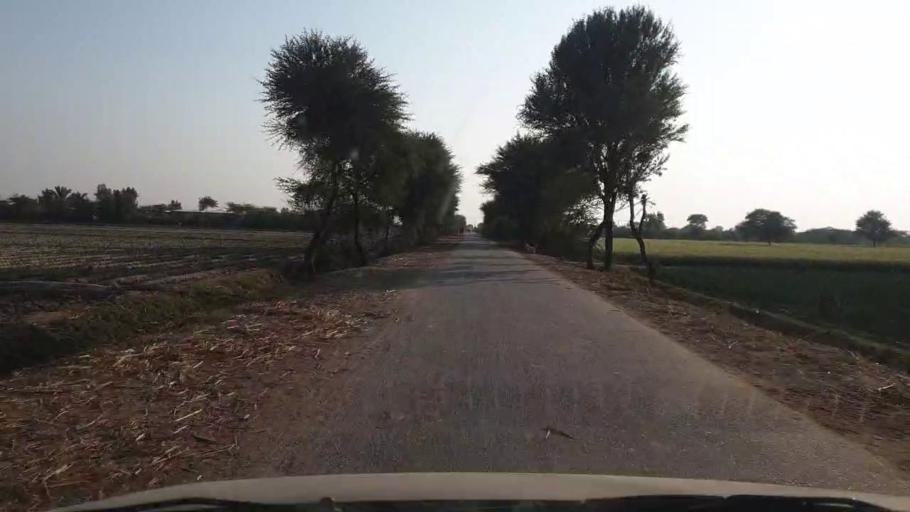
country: PK
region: Sindh
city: Samaro
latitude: 25.2664
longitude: 69.3603
